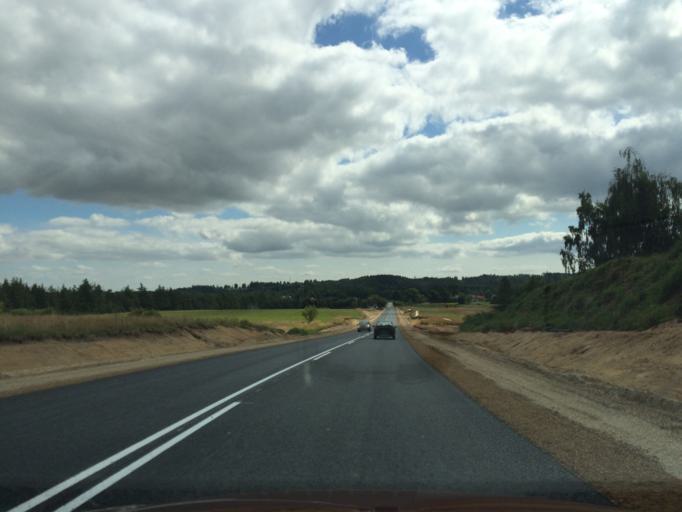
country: DK
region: Central Jutland
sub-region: Silkeborg Kommune
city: Svejbaek
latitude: 56.1866
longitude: 9.6328
